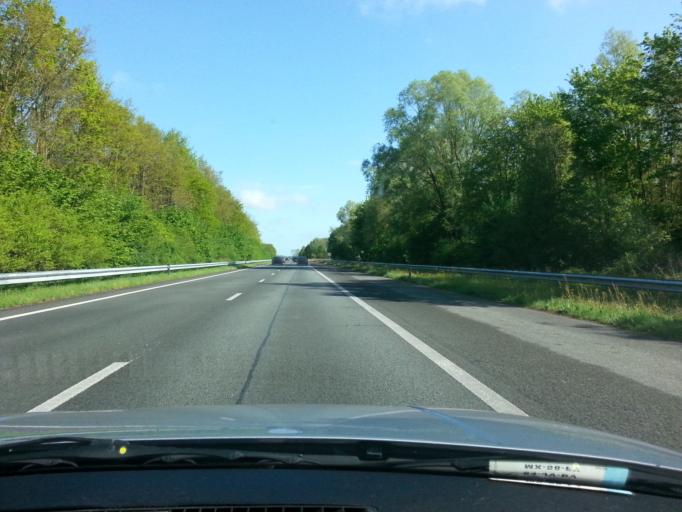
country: NL
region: Flevoland
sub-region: Gemeente Noordoostpolder
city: Emmeloord
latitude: 52.7417
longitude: 5.7693
